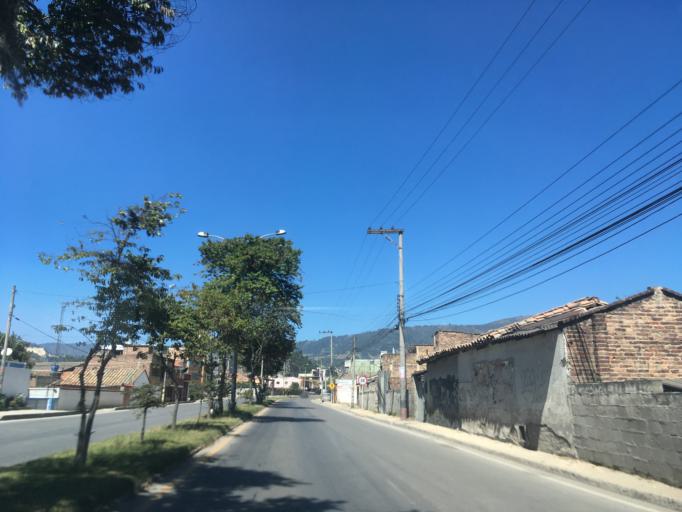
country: CO
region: Boyaca
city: Duitama
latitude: 5.8175
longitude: -73.0219
